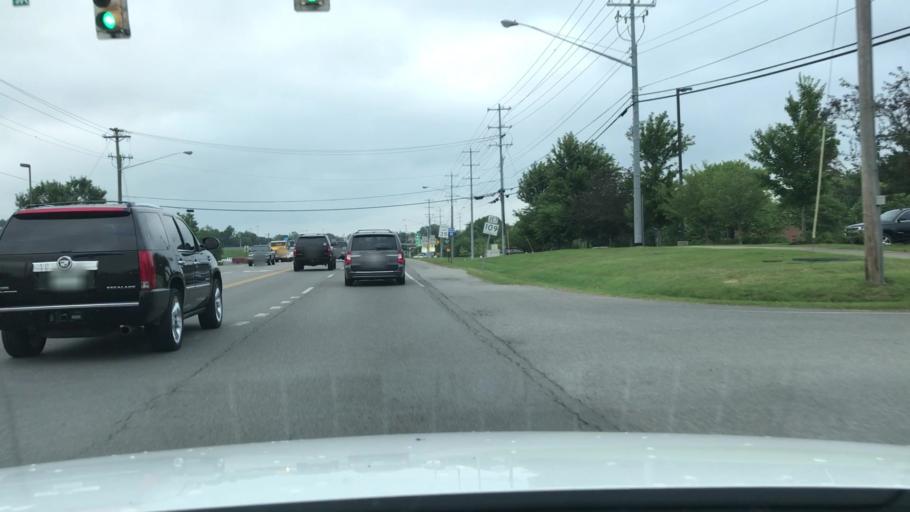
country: US
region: Tennessee
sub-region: Sumner County
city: Gallatin
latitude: 36.3763
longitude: -86.4723
